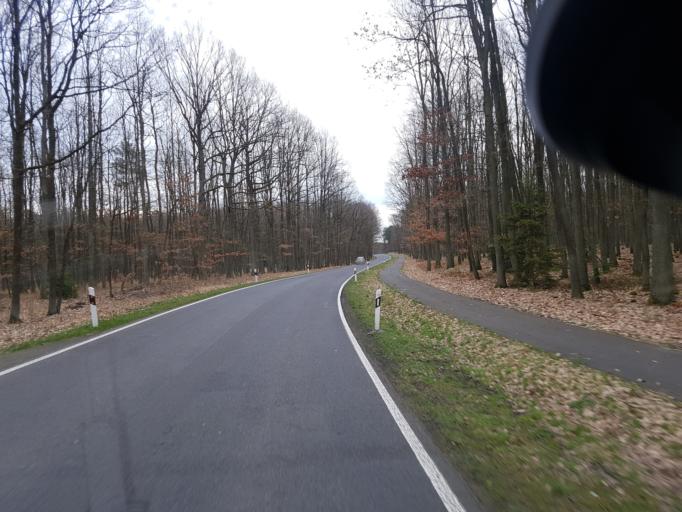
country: DE
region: Brandenburg
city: Gross Lindow
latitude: 52.1701
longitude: 14.4940
